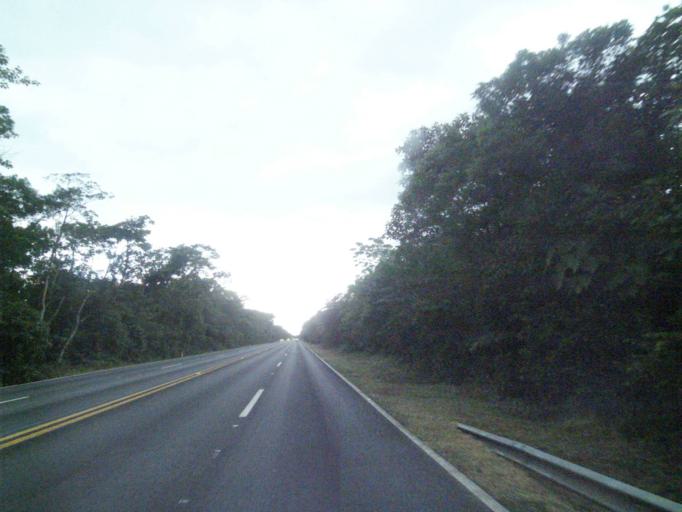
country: BR
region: Parana
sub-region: Guaratuba
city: Guaratuba
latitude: -25.7689
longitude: -48.5841
